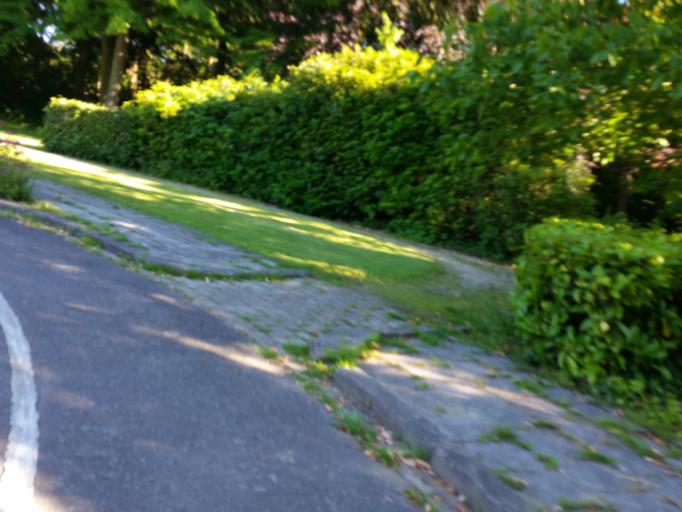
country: BE
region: Flanders
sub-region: Provincie Antwerpen
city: Mechelen
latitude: 51.0173
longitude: 4.4590
